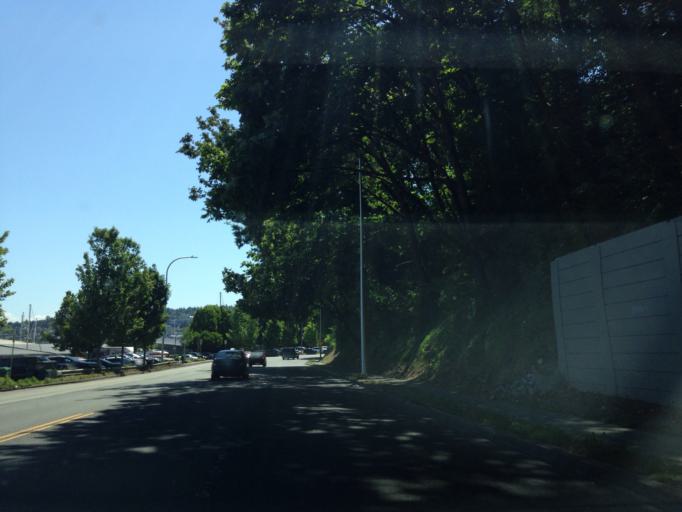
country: US
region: Washington
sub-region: King County
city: Seattle
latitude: 47.6444
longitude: -122.3461
